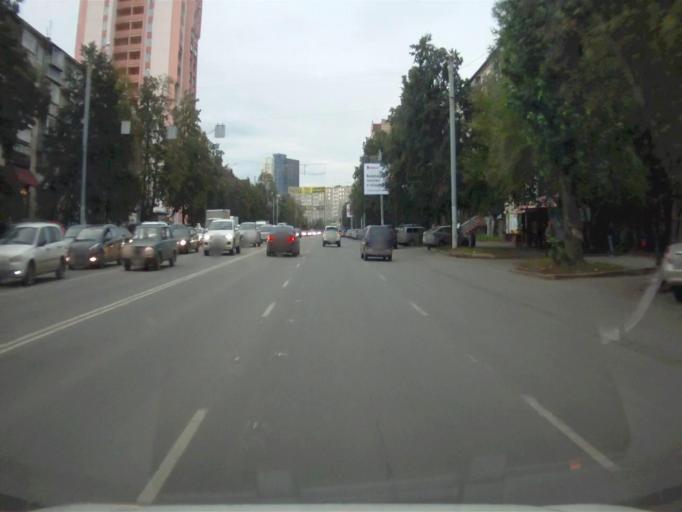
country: RU
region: Chelyabinsk
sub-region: Gorod Chelyabinsk
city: Chelyabinsk
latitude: 55.1575
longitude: 61.3813
